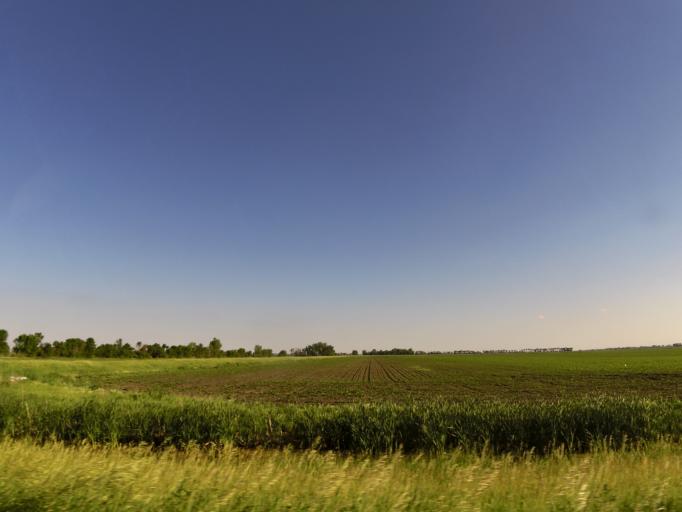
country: US
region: North Dakota
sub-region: Grand Forks County
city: Grand Forks Air Force Base
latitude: 48.1358
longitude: -97.2350
